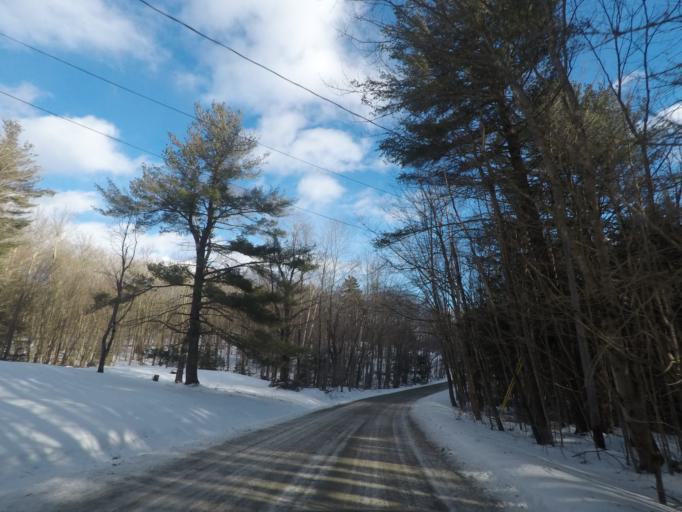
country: US
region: New York
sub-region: Rensselaer County
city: Poestenkill
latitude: 42.7417
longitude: -73.4739
